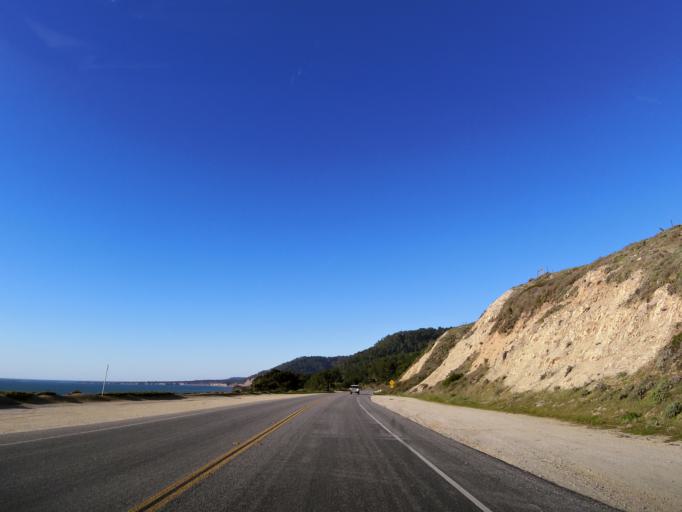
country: US
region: California
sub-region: Santa Cruz County
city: Bonny Doon
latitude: 37.0750
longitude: -122.2615
